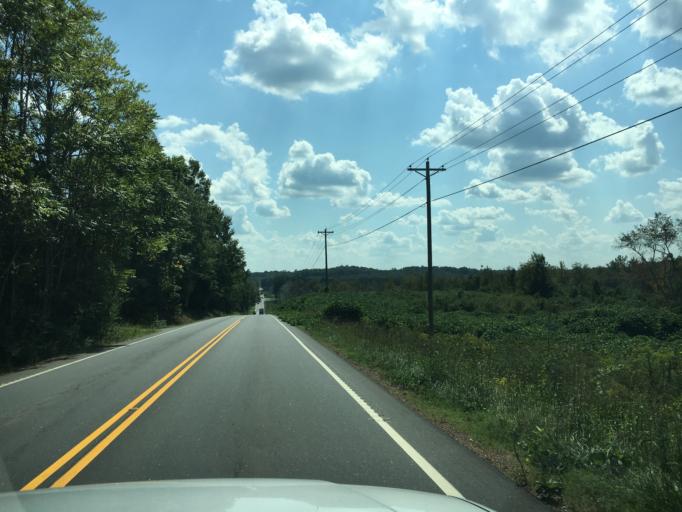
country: US
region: South Carolina
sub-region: Greenville County
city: Fountain Inn
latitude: 34.6317
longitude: -82.0967
